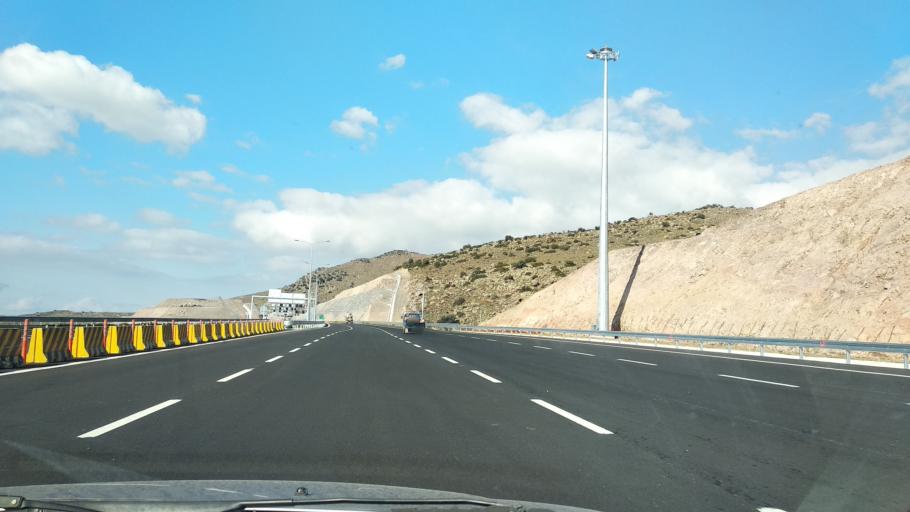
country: TR
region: Izmir
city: Menemen
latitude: 38.6742
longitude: 27.0624
